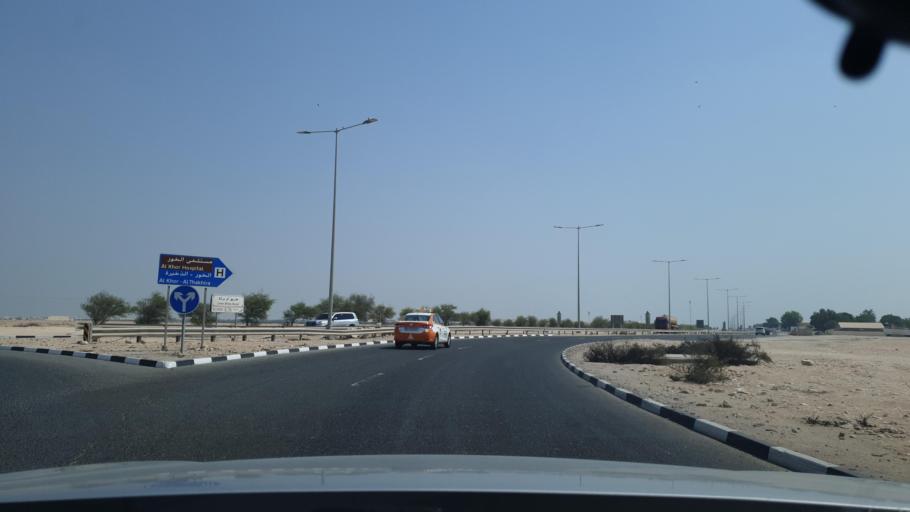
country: QA
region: Al Khawr
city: Al Khawr
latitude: 25.7210
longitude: 51.4997
